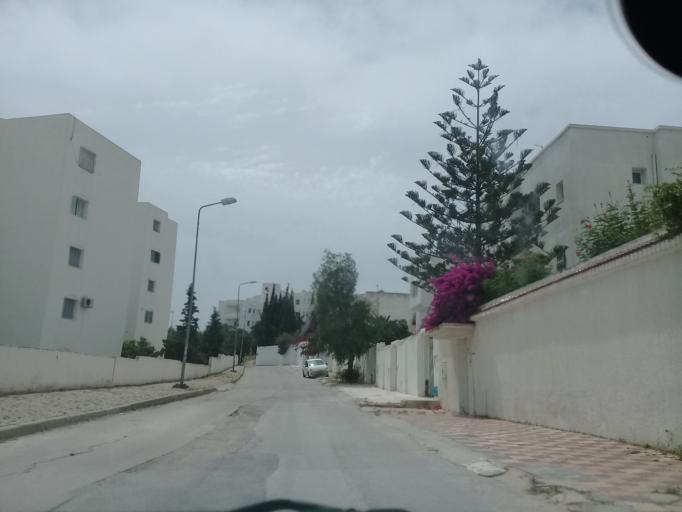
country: TN
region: Tunis
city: Tunis
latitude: 36.8375
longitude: 10.1528
